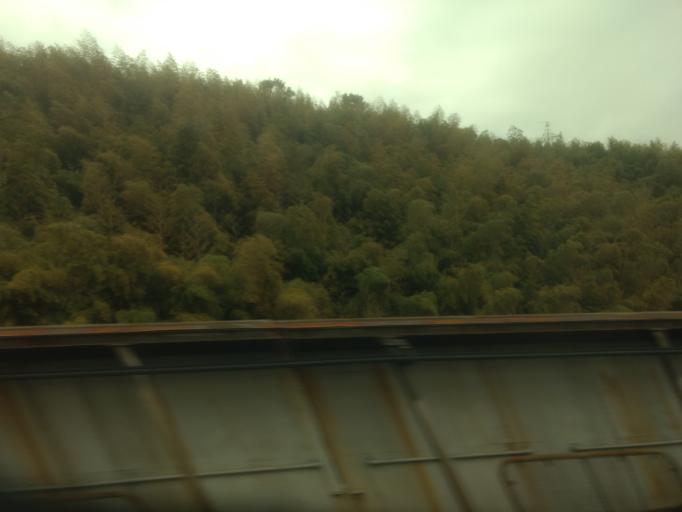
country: JP
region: Yamaguchi
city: Kudamatsu
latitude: 34.0356
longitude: 131.8577
